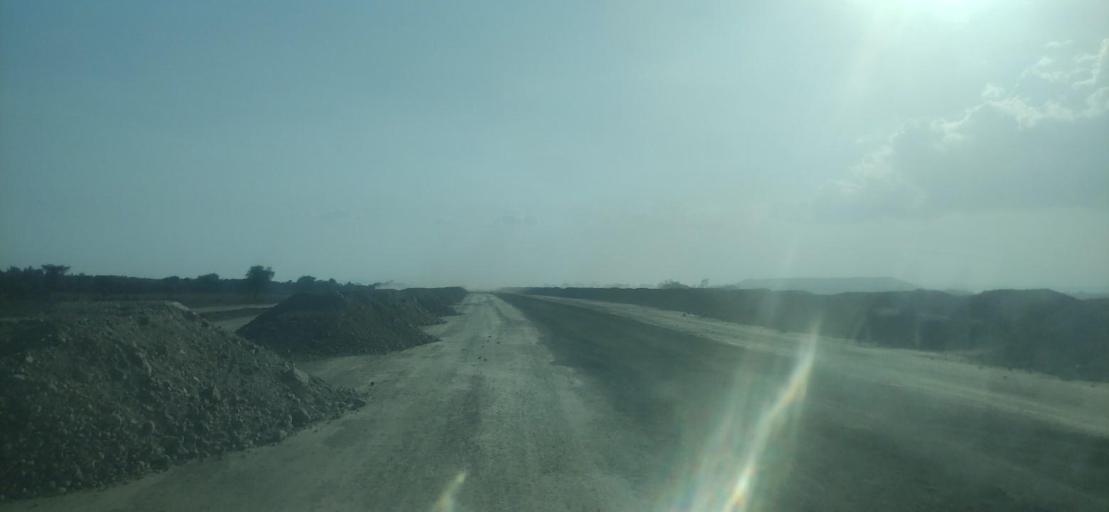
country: ET
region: Southern Nations, Nationalities, and People's Region
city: Hawassa
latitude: 7.1711
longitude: 38.4893
